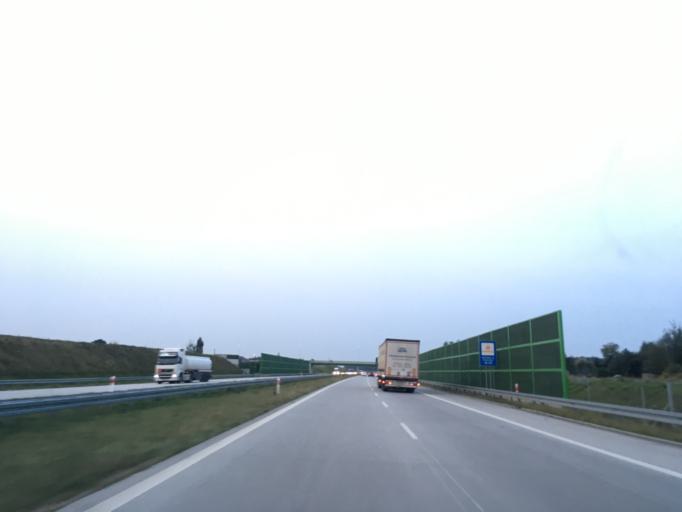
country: PL
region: Lodz Voivodeship
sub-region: Powiat lodzki wschodni
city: Andrespol
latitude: 51.7822
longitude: 19.6107
